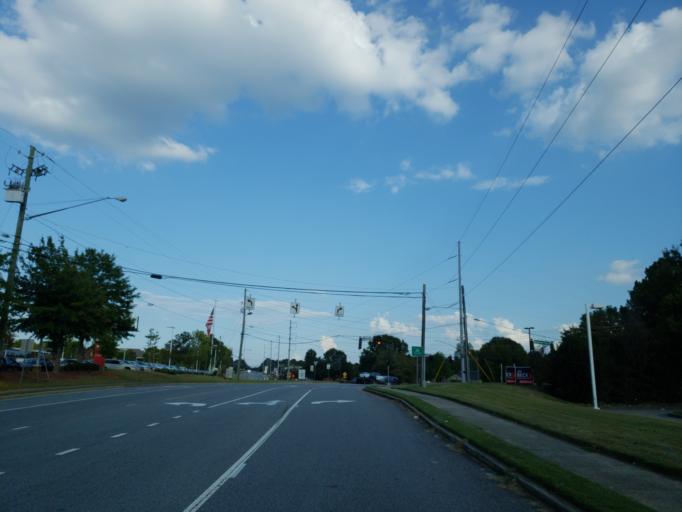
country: US
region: Georgia
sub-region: Fulton County
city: Alpharetta
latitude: 34.0664
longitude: -84.3194
